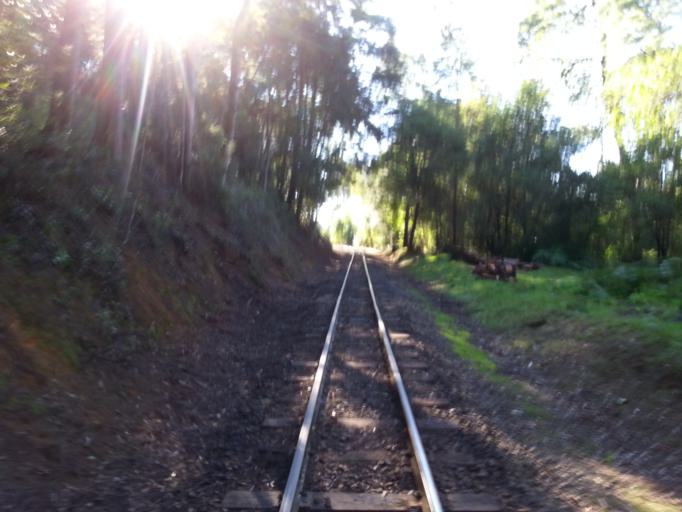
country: AU
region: Victoria
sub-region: Cardinia
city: Emerald
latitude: -37.9339
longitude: 145.4591
